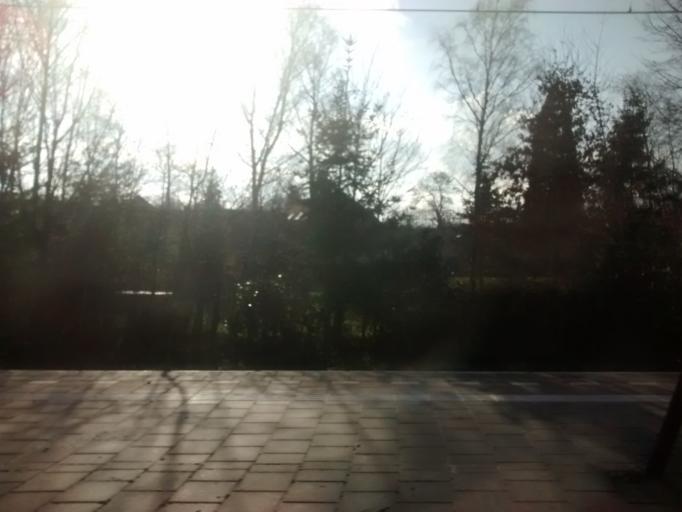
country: NL
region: Limburg
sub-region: Gemeente Schinnen
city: Schinnen
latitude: 50.9387
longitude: 5.8768
